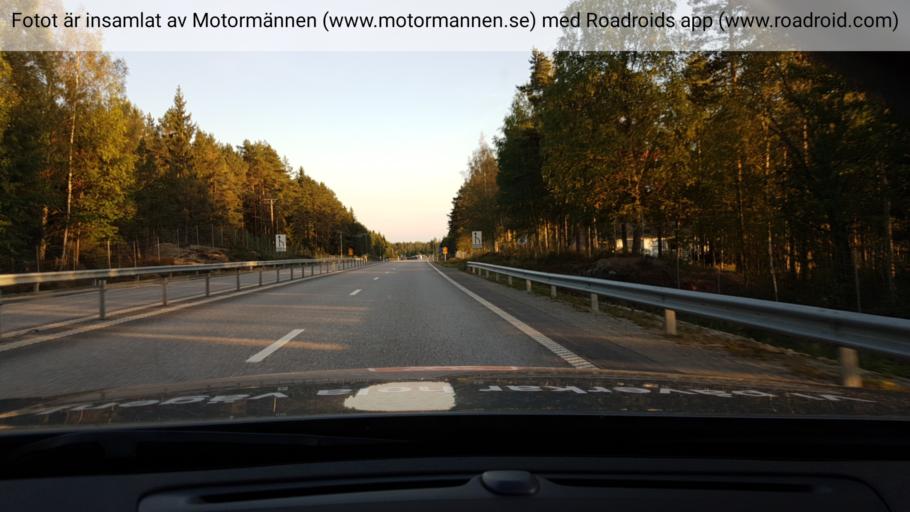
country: SE
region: Vaestmanland
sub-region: Surahammars Kommun
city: Surahammar
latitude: 59.7051
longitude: 16.2470
